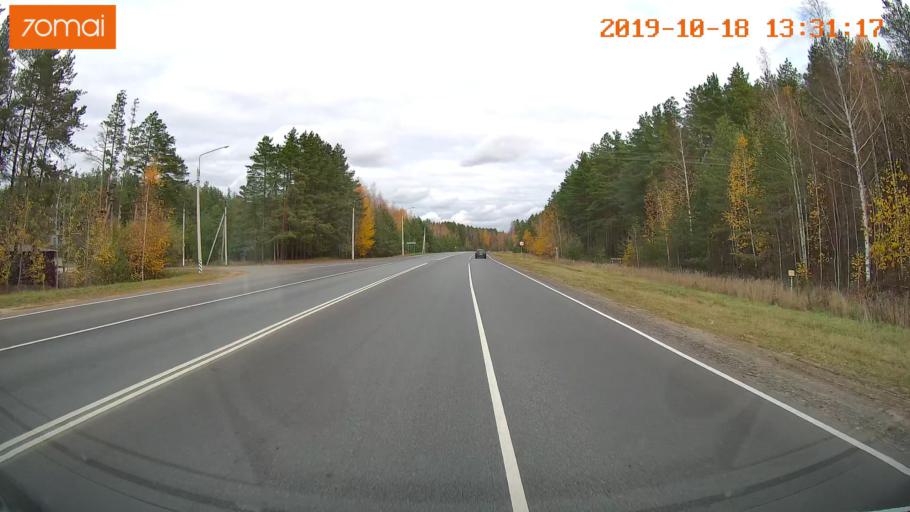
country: RU
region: Rjazan
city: Solotcha
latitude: 54.8207
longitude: 39.8976
